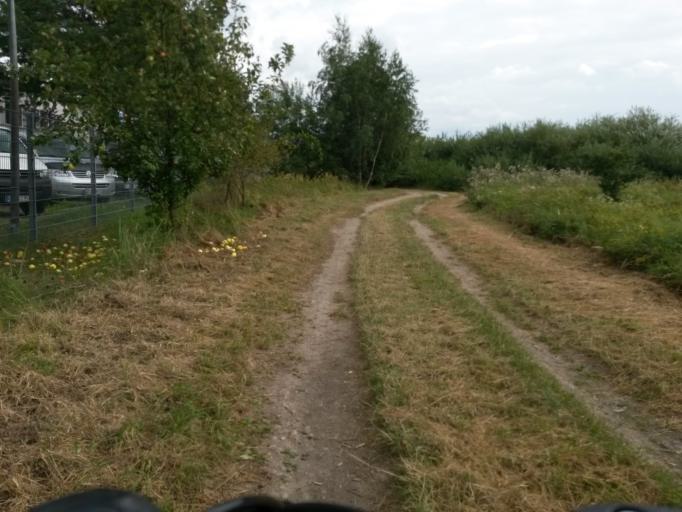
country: DE
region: Brandenburg
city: Angermunde
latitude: 53.0249
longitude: 13.9863
